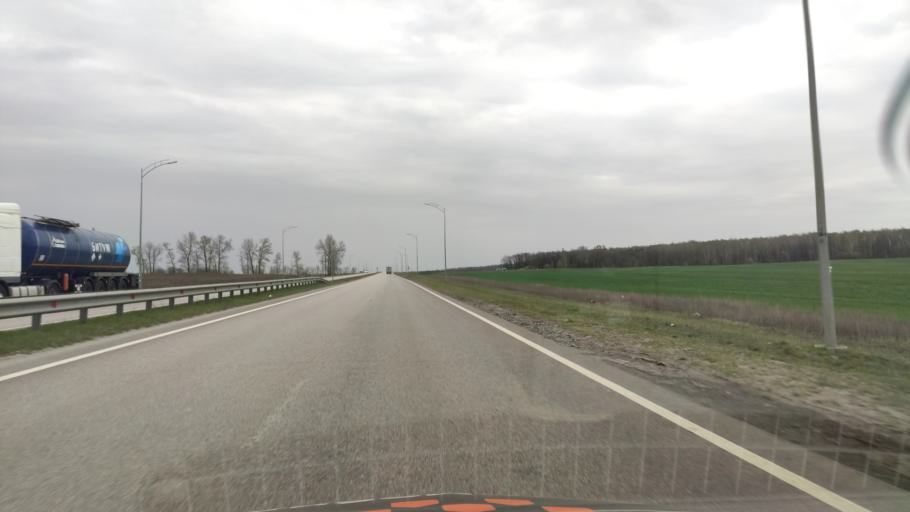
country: RU
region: Belgorod
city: Staryy Oskol
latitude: 51.4131
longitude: 37.8854
